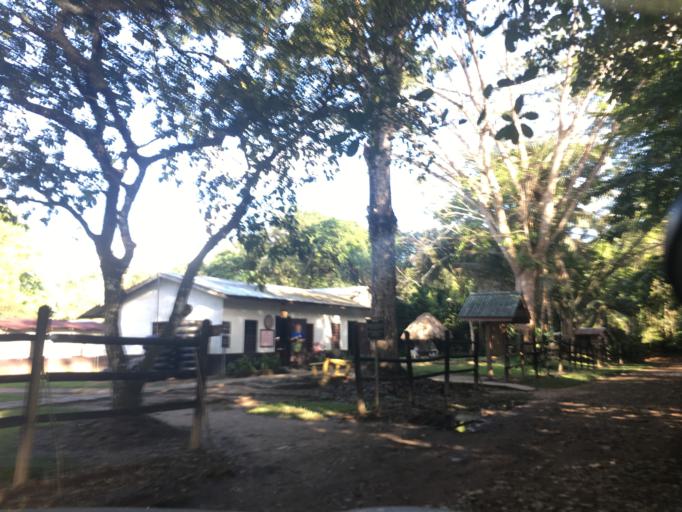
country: BZ
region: Stann Creek
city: Placencia
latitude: 16.7807
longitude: -88.4590
